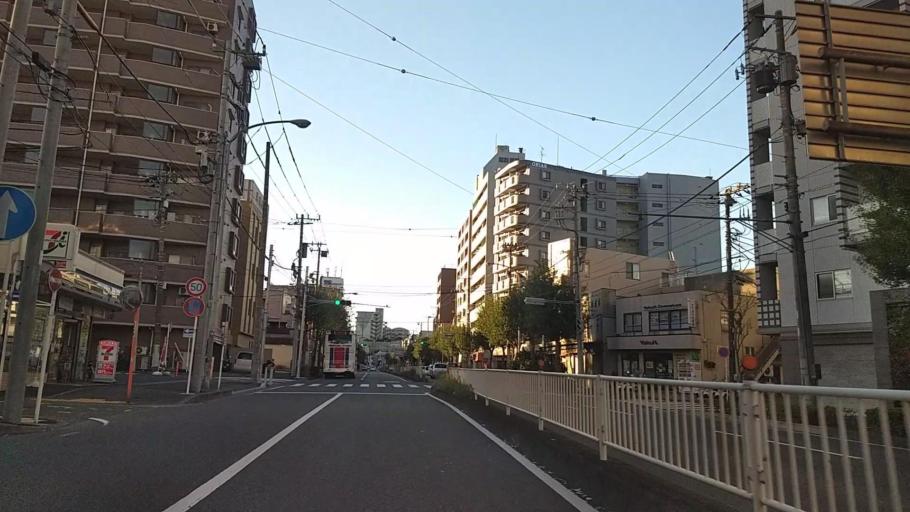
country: JP
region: Kanagawa
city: Yokohama
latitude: 35.4532
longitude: 139.6129
